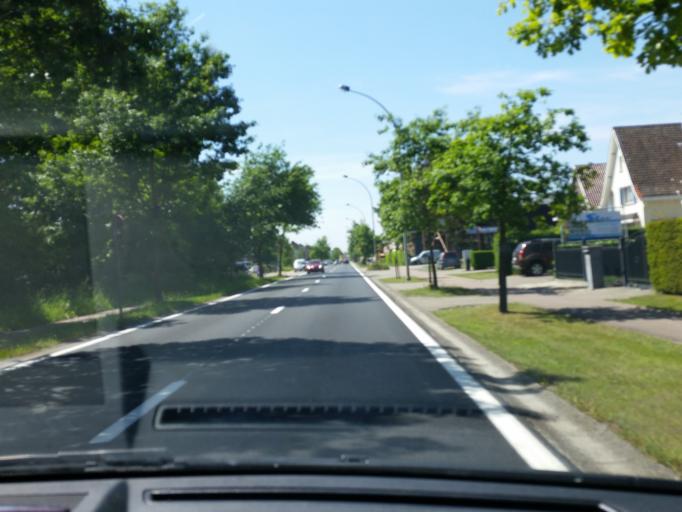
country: BE
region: Flanders
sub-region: Provincie Antwerpen
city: Bonheiden
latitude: 51.0354
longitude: 4.5255
